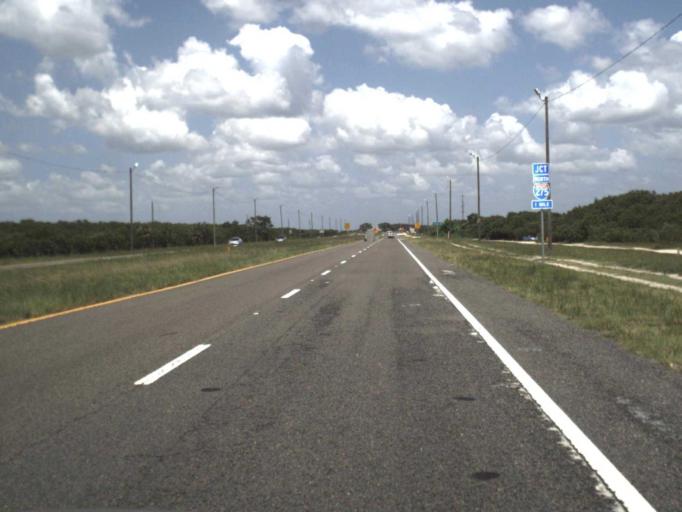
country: US
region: Florida
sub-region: Pinellas County
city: Feather Sound
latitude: 27.8884
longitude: -82.6388
